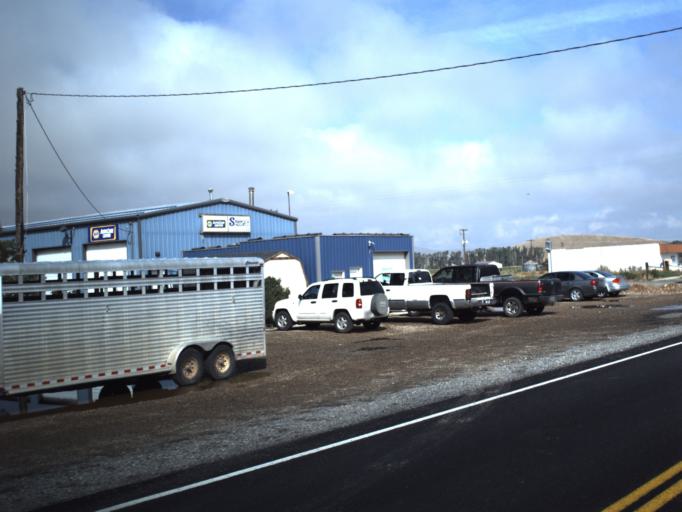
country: US
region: Utah
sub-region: Rich County
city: Randolph
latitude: 41.5235
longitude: -111.1629
